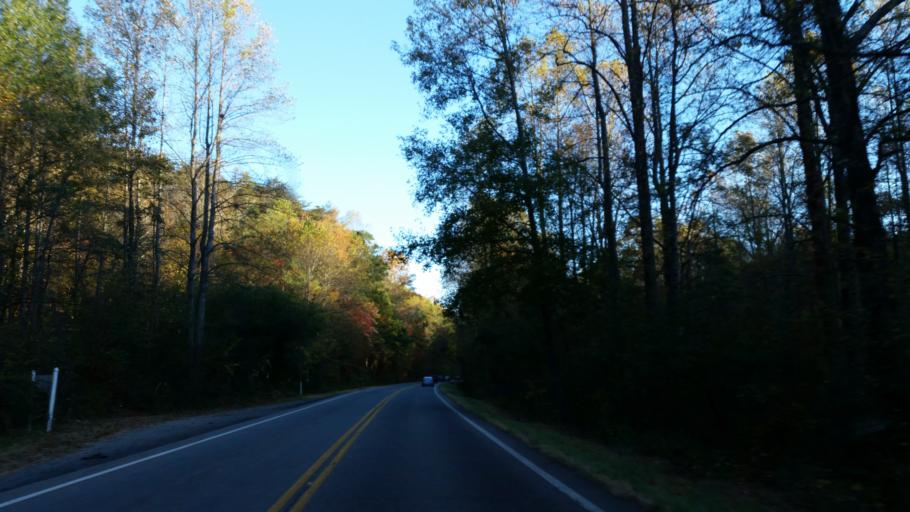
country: US
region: Georgia
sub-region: Pickens County
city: Jasper
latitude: 34.5604
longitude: -84.3000
